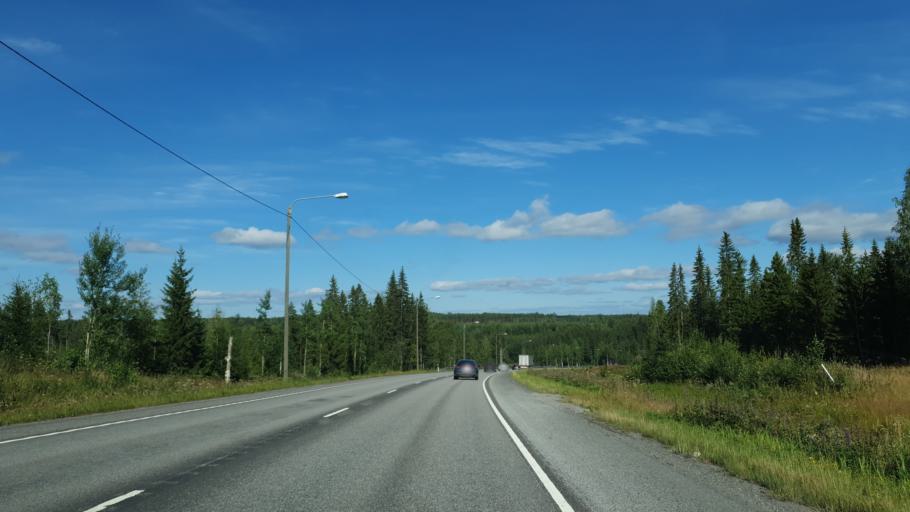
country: FI
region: Central Finland
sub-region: Jyvaeskylae
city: Toivakka
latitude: 62.2520
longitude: 26.0638
